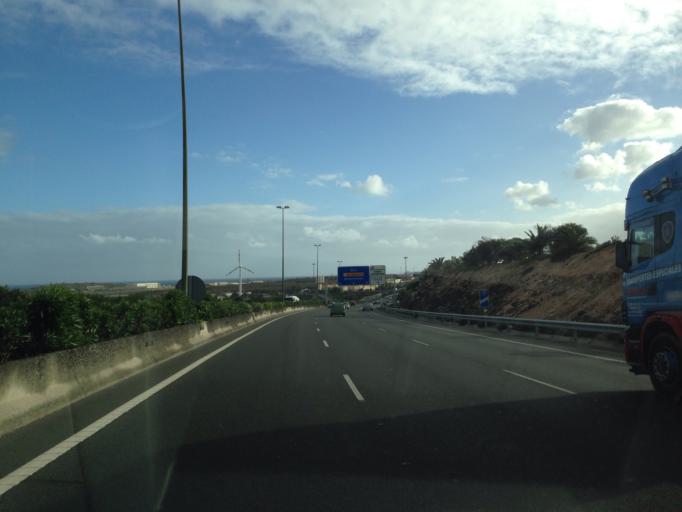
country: ES
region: Canary Islands
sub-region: Provincia de Las Palmas
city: Telde
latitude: 27.9557
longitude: -15.3878
